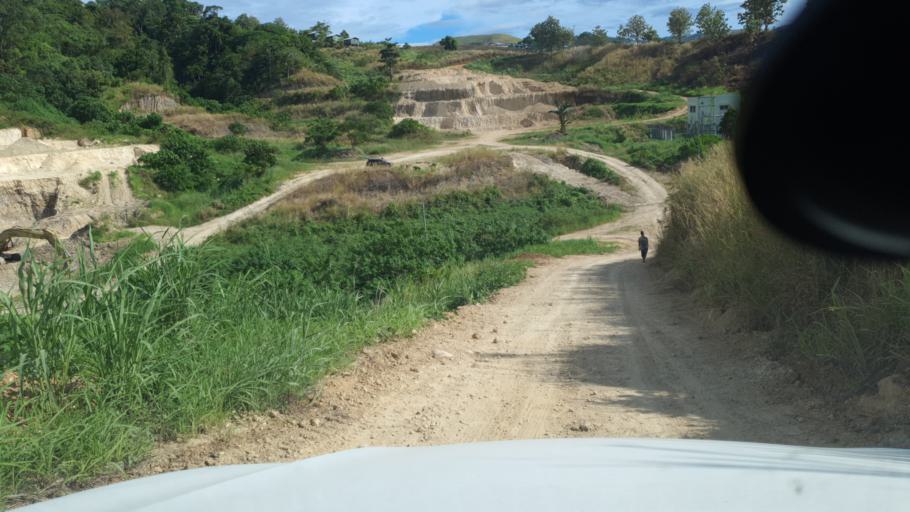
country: SB
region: Guadalcanal
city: Honiara
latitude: -9.4364
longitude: 159.9288
